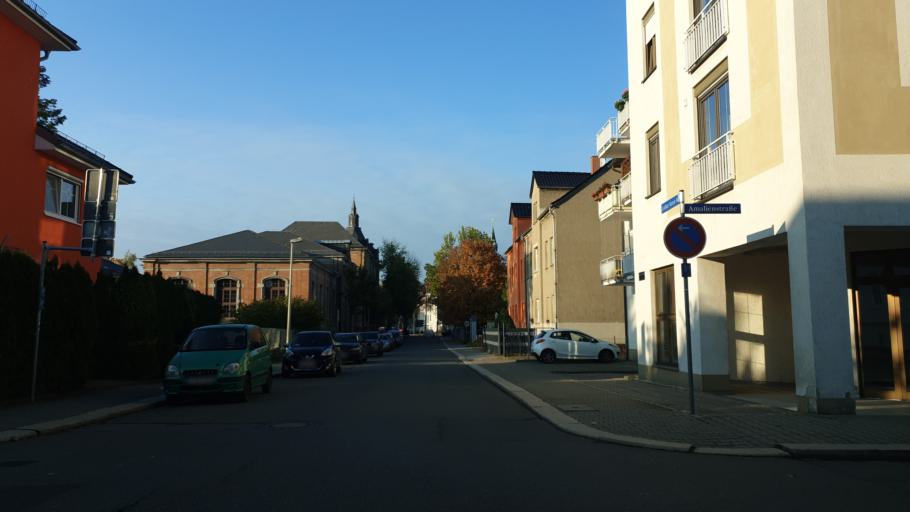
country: DE
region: Saxony
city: Zwickau
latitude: 50.7132
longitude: 12.4957
